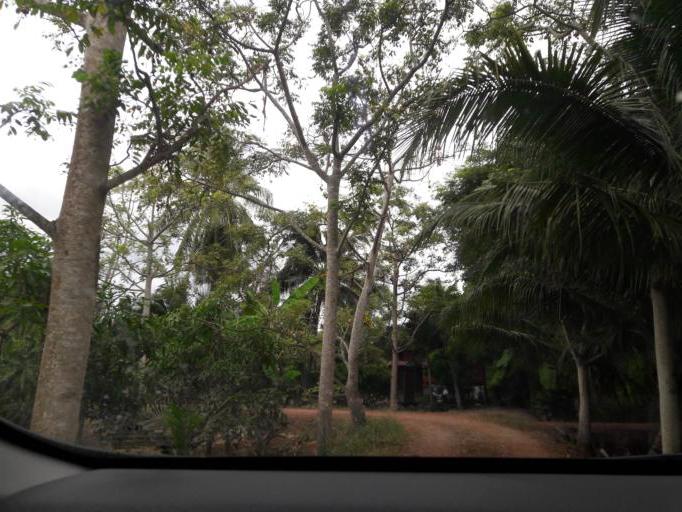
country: TH
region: Ratchaburi
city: Damnoen Saduak
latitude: 13.5590
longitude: 99.9948
